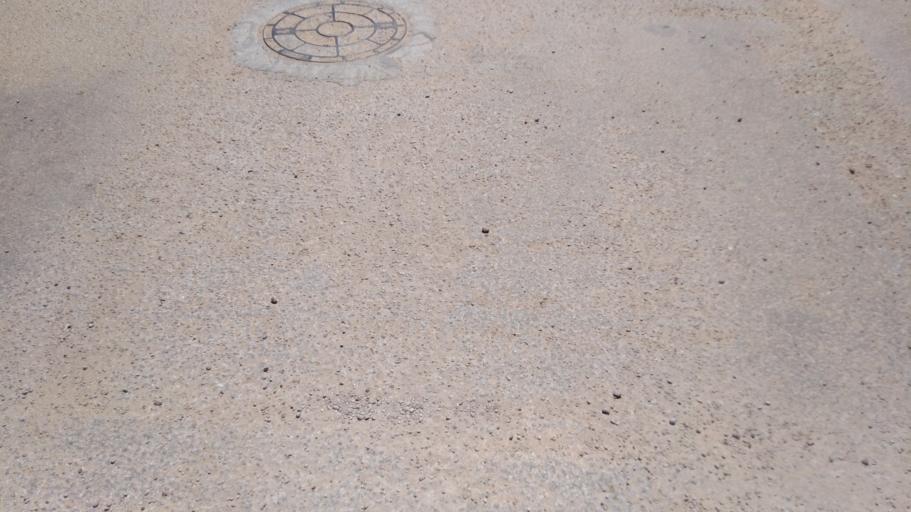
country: TN
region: Qabis
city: Matmata
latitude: 33.6124
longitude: 10.2912
